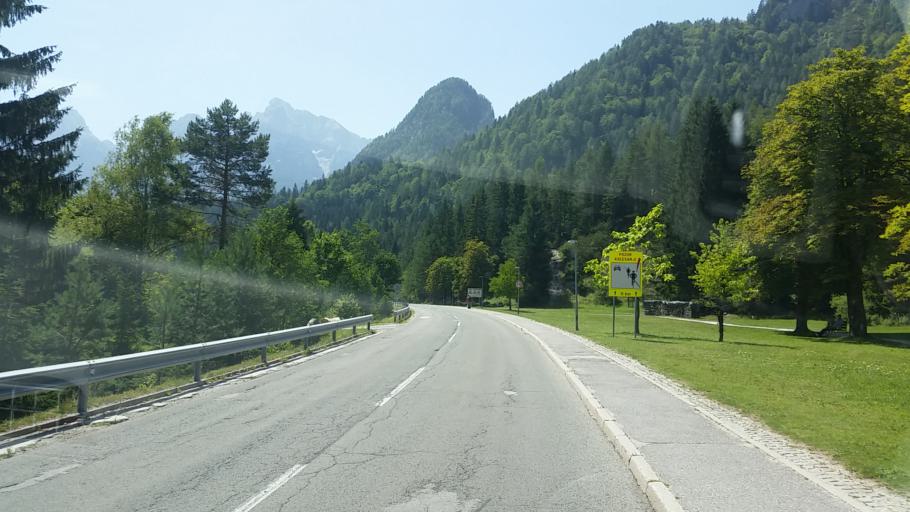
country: SI
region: Kranjska Gora
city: Kranjska Gora
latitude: 46.4805
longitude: 13.7812
